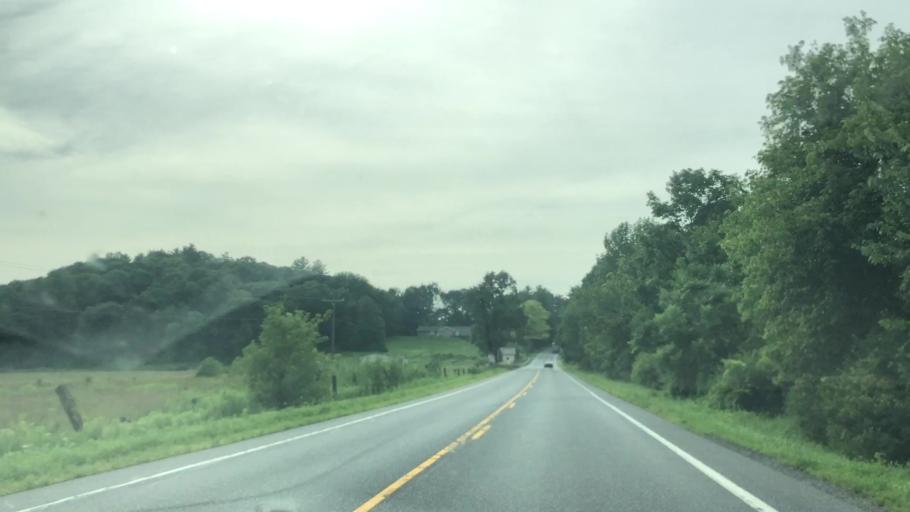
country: US
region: New York
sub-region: Warren County
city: Queensbury
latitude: 43.4063
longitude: -73.5479
